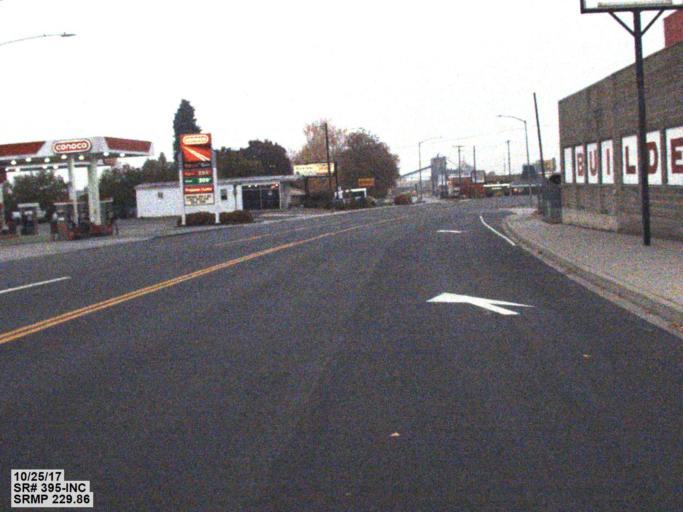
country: US
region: Washington
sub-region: Stevens County
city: Colville
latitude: 48.5486
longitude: -117.9079
